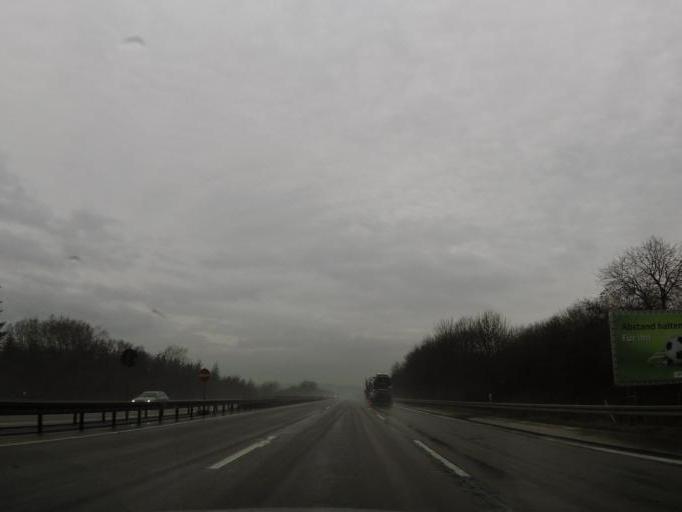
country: DE
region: Hesse
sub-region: Regierungsbezirk Giessen
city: Villmar
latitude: 50.3300
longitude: 8.2058
